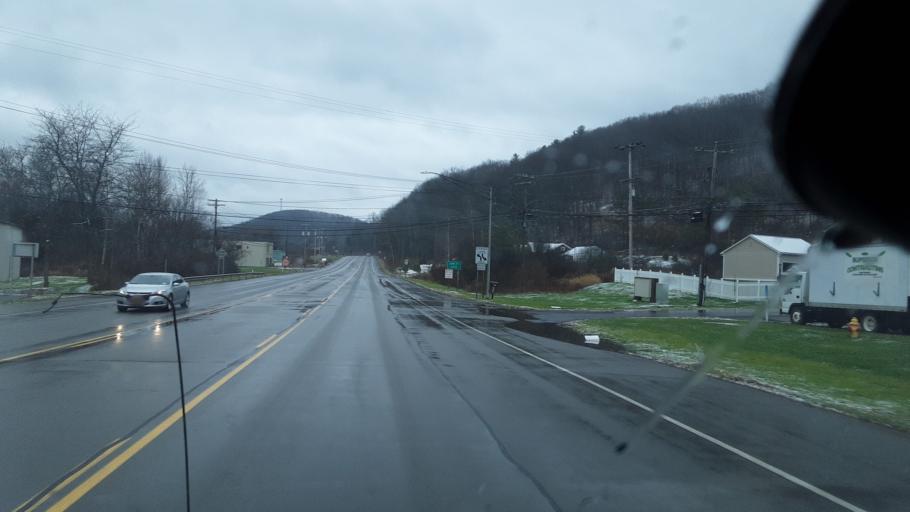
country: US
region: New York
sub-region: Cattaraugus County
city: Olean
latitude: 42.1012
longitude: -78.4220
